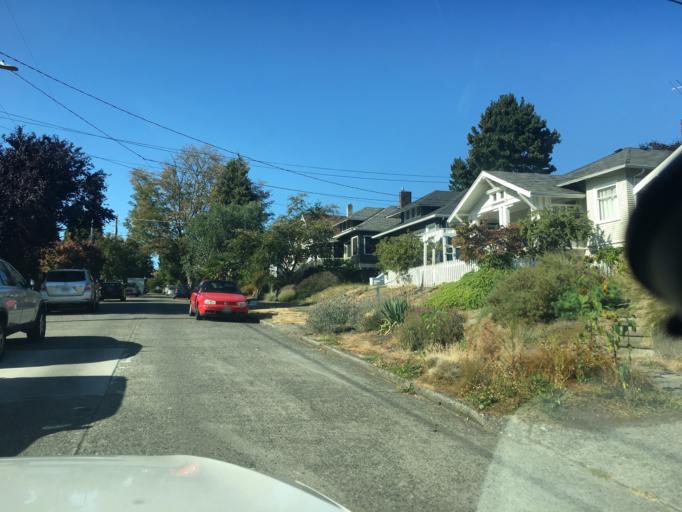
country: US
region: Washington
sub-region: King County
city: Shoreline
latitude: 47.6781
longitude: -122.3864
